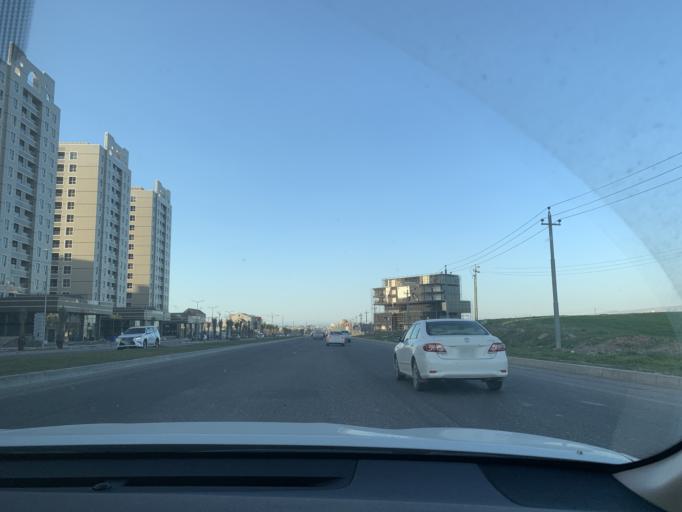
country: IQ
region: Arbil
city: Erbil
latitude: 36.2599
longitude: 44.0144
